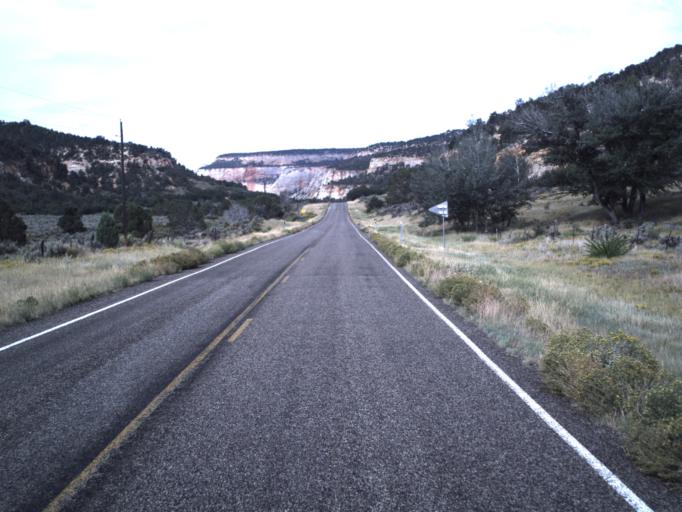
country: US
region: Utah
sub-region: Washington County
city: Hildale
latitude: 37.2384
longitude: -112.8370
